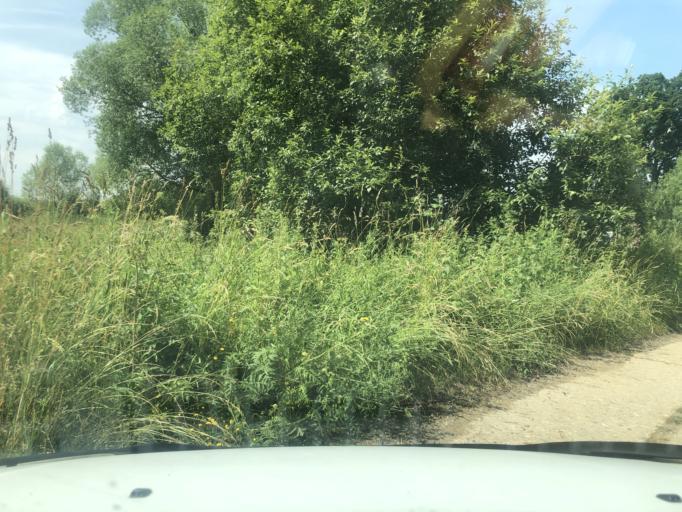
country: RU
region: Jaroslavl
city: Pereslavl'-Zalesskiy
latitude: 57.0454
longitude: 38.8667
